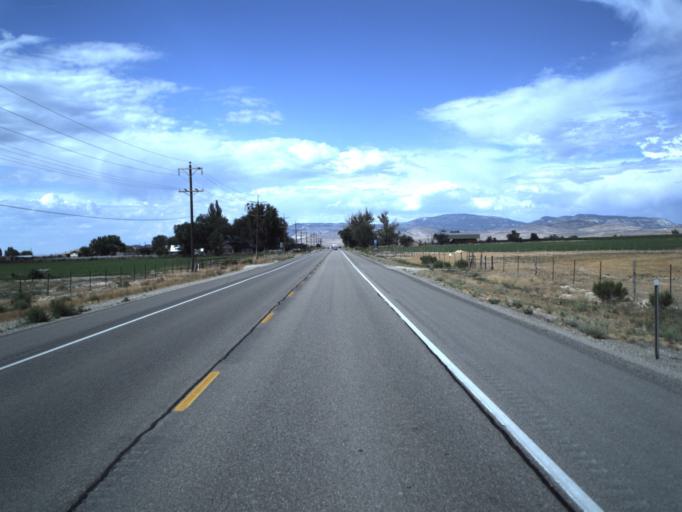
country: US
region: Utah
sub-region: Sanpete County
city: Centerfield
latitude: 39.0878
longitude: -111.8201
